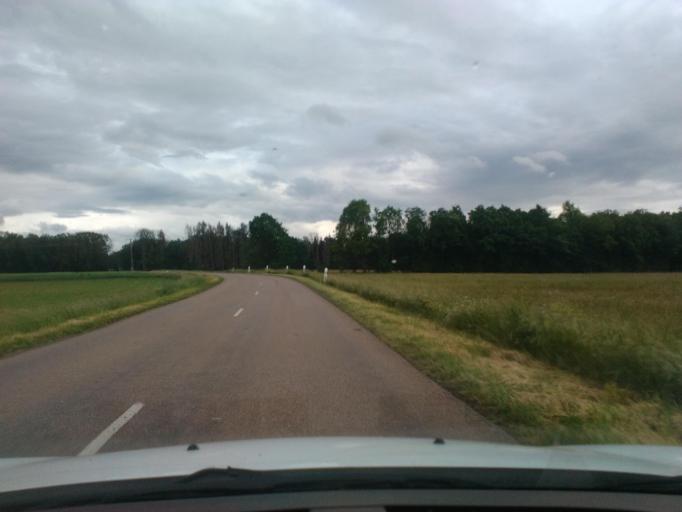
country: FR
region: Lorraine
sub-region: Departement de Meurthe-et-Moselle
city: Gerbeviller
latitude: 48.4272
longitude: 6.5798
